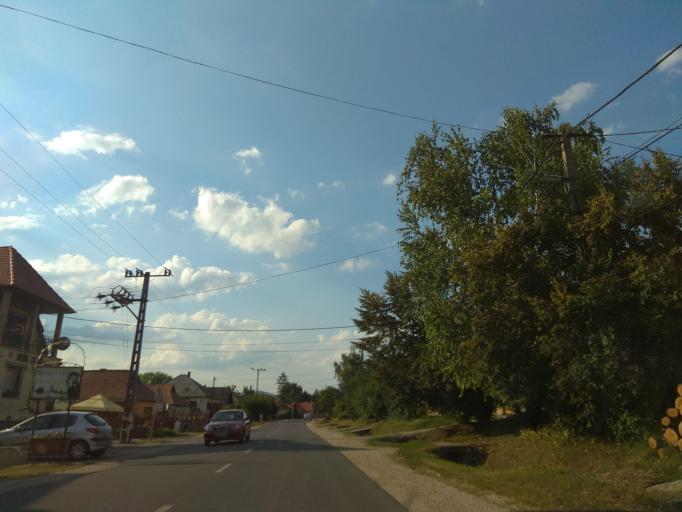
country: HU
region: Borsod-Abauj-Zemplen
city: Harsany
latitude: 47.9664
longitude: 20.7418
